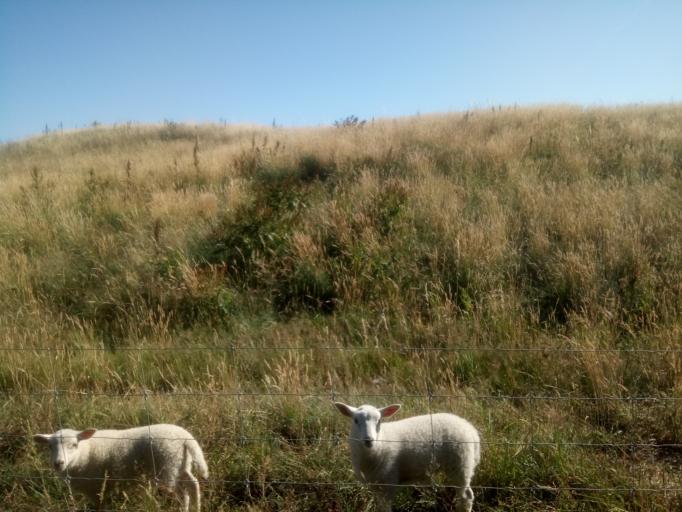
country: DK
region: Central Jutland
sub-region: Herning Kommune
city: Herning
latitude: 56.1525
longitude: 8.9774
